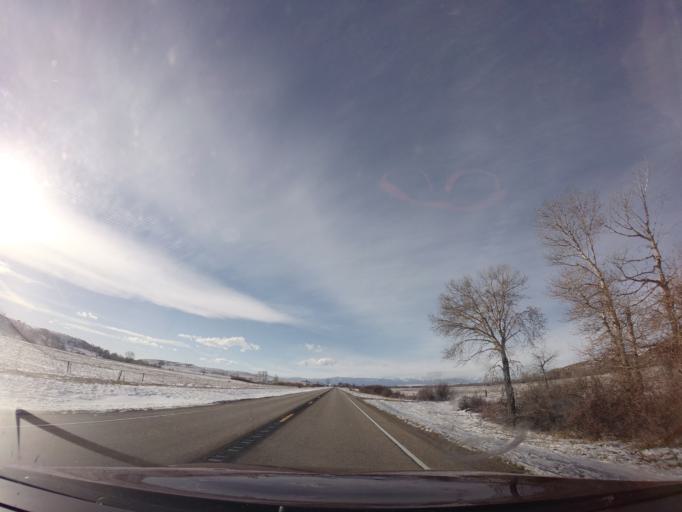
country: US
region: Montana
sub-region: Stillwater County
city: Columbus
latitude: 45.4198
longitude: -109.1095
